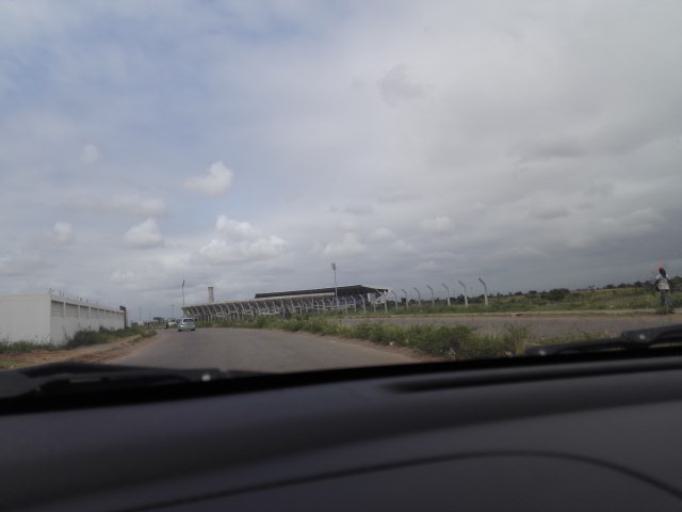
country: MZ
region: Maputo City
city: Maputo
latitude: -25.8239
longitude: 32.5814
